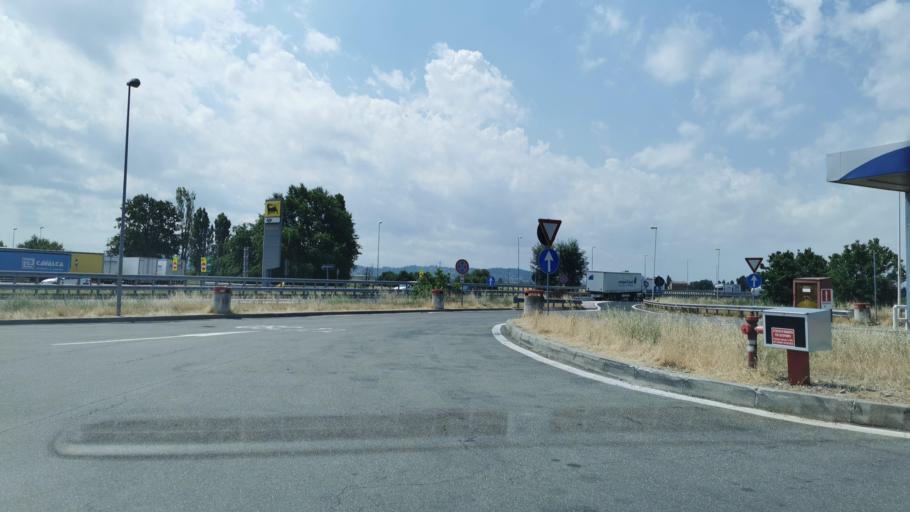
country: IT
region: Piedmont
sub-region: Provincia di Alessandria
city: Tortona
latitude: 44.9351
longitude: 8.8835
